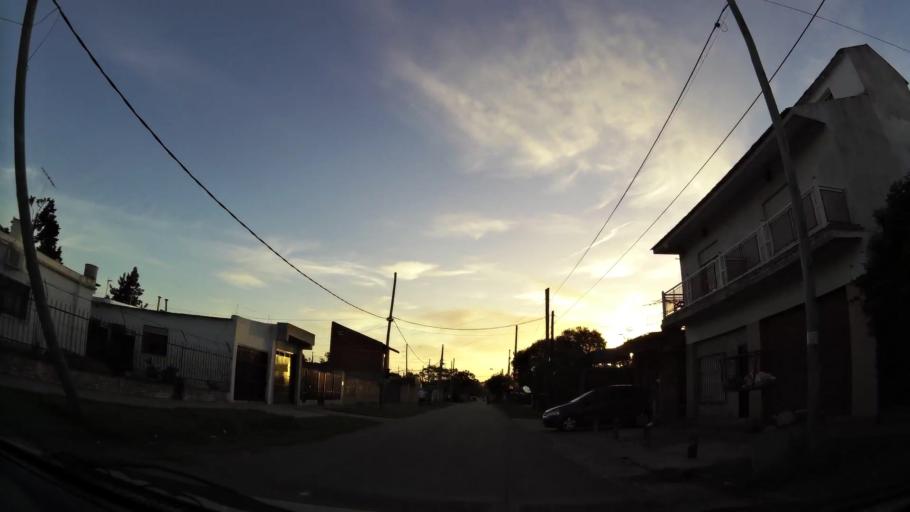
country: AR
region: Buenos Aires
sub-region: Partido de Quilmes
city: Quilmes
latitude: -34.7834
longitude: -58.2266
